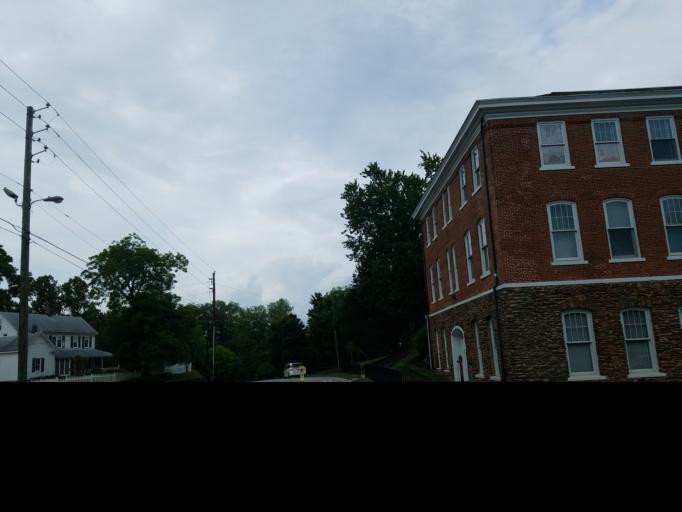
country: US
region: Georgia
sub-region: Lumpkin County
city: Dahlonega
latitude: 34.5296
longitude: -83.9880
